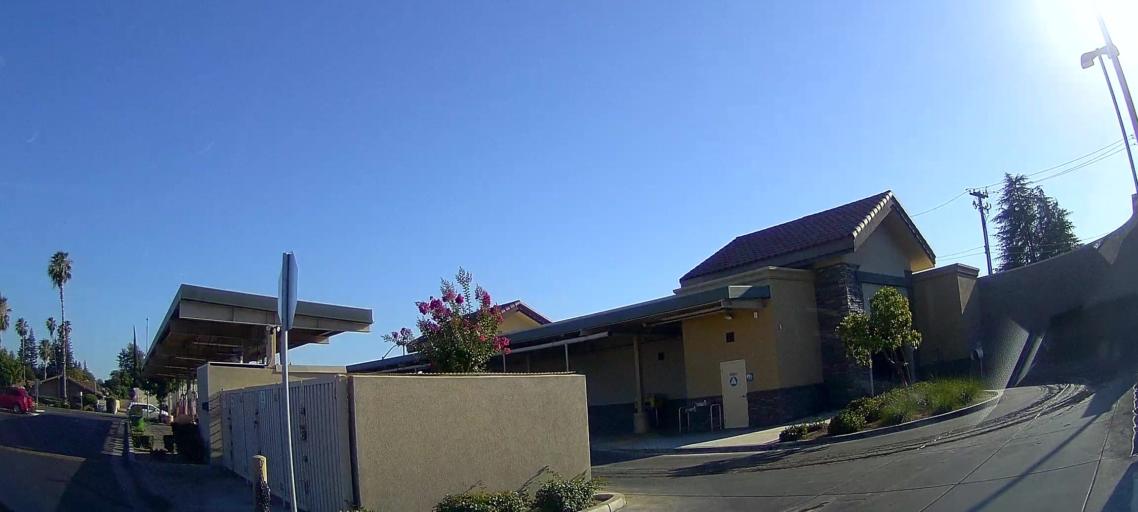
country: US
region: California
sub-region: Fresno County
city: Fresno
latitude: 36.8236
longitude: -119.8079
